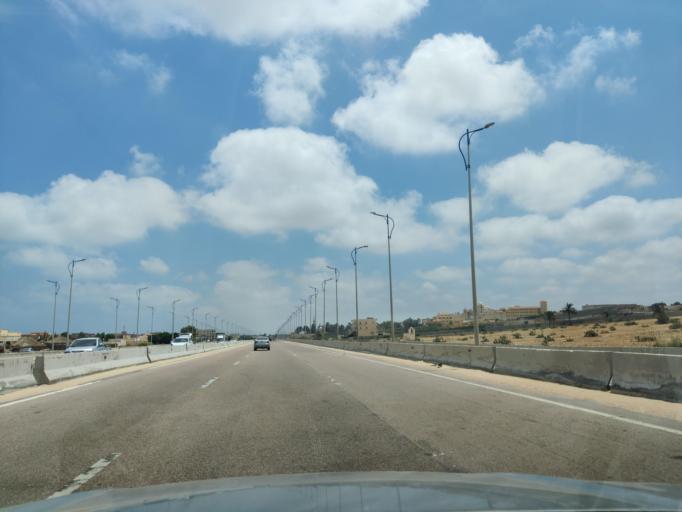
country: EG
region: Alexandria
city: Alexandria
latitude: 30.9815
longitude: 29.5791
